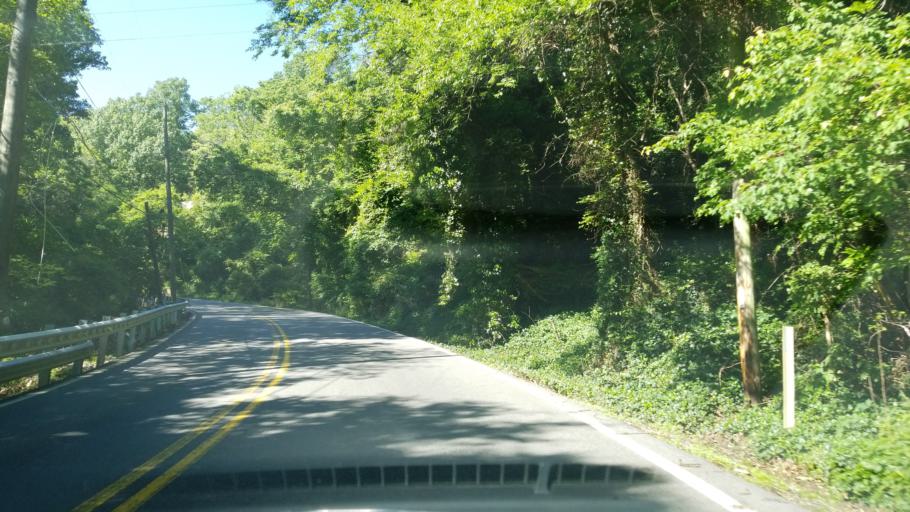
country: US
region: Tennessee
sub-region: Hamilton County
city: Lookout Mountain
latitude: 35.0124
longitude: -85.3378
